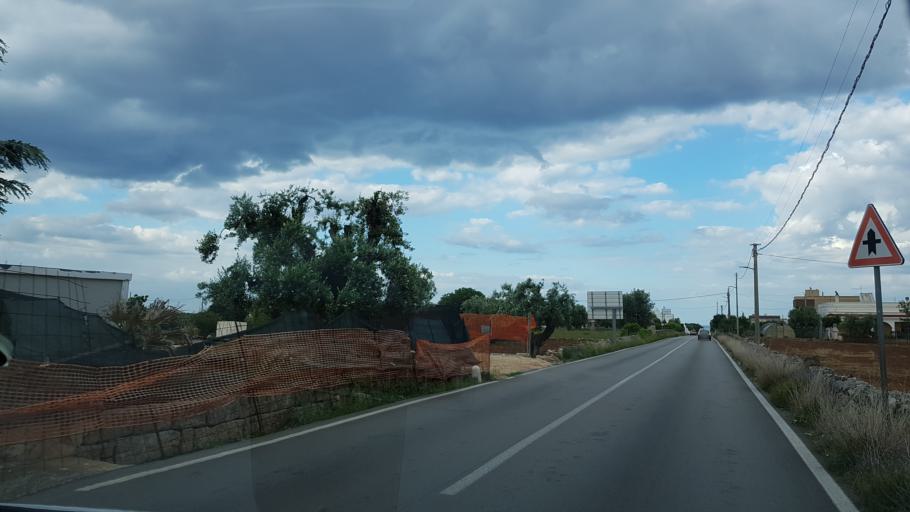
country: IT
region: Apulia
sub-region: Provincia di Brindisi
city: Fasano
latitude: 40.8431
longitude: 17.3764
